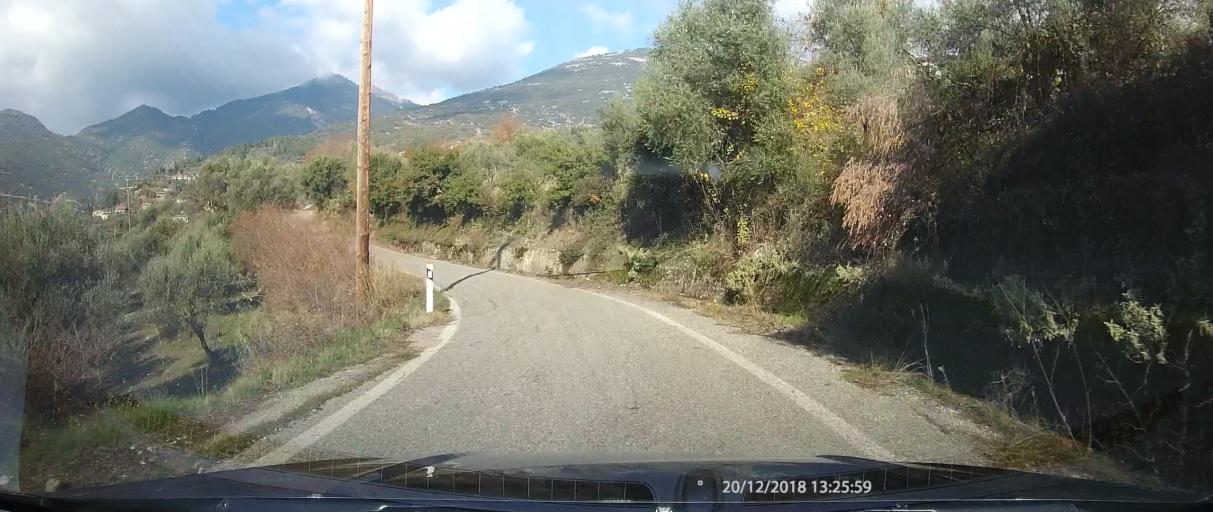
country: GR
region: West Greece
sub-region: Nomos Aitolias kai Akarnanias
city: Paravola
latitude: 38.6260
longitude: 21.5650
